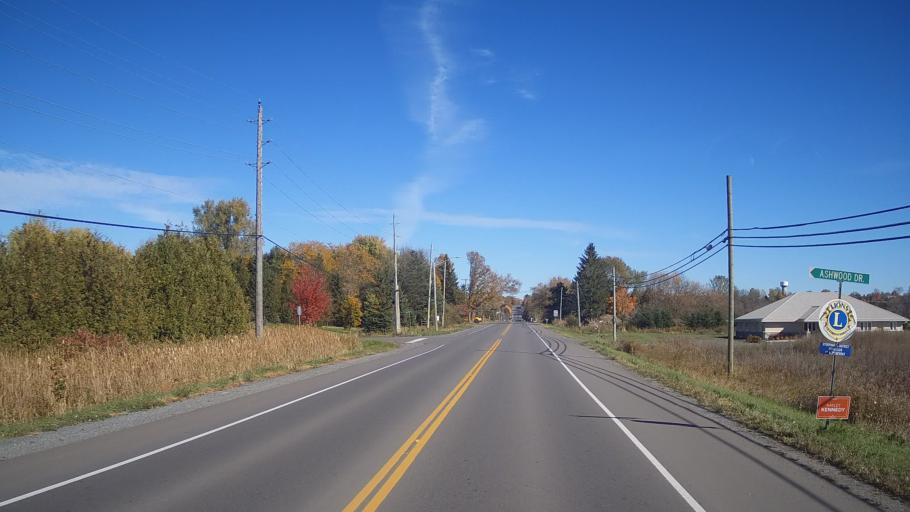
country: CA
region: Ontario
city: Kingston
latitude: 44.4065
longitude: -76.6118
